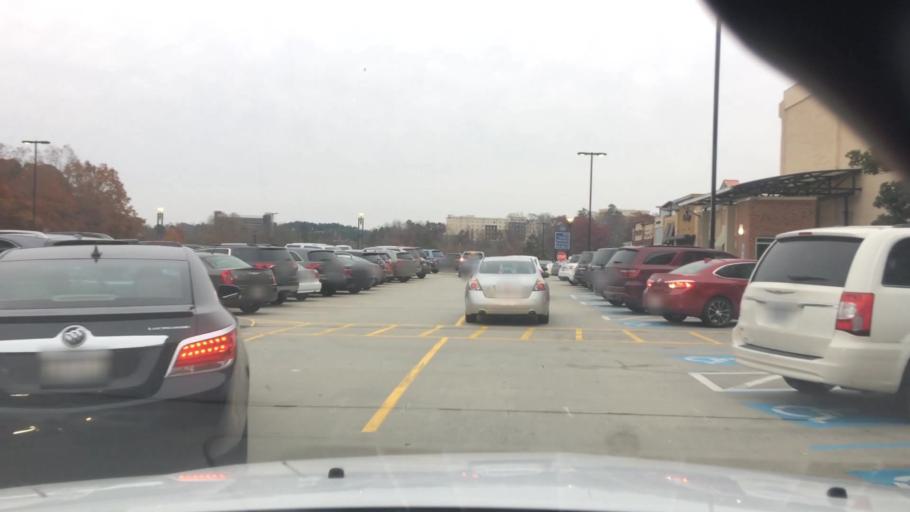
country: US
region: North Carolina
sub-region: Wake County
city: West Raleigh
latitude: 35.8398
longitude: -78.6780
